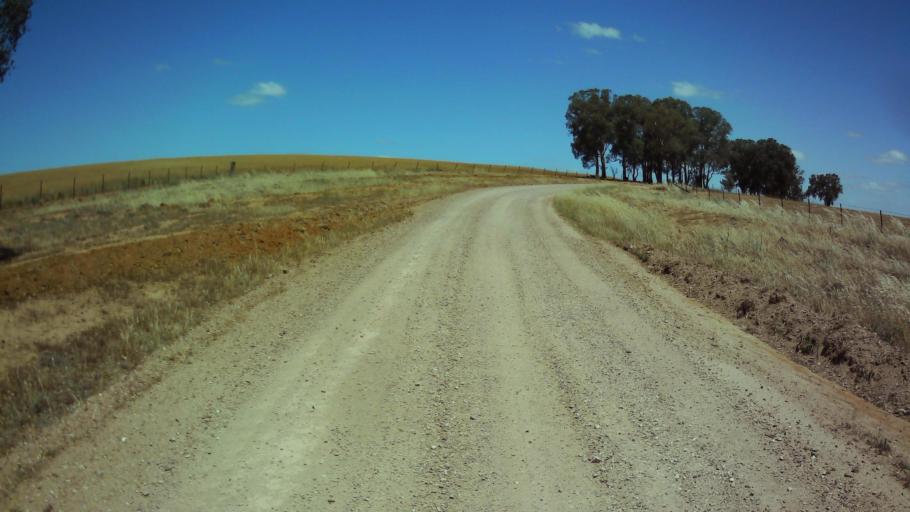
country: AU
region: New South Wales
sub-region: Weddin
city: Grenfell
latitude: -33.9398
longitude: 148.3297
